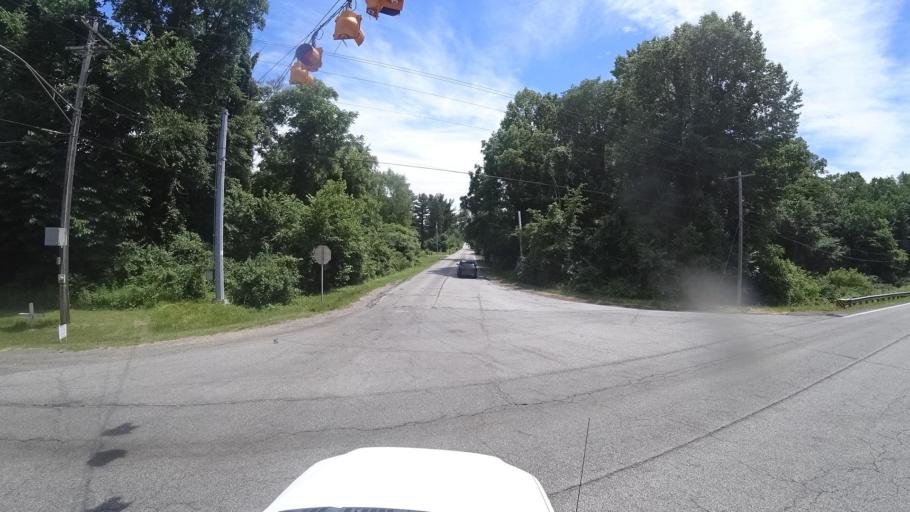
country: US
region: Indiana
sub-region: Porter County
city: Porter
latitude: 41.6276
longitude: -87.0770
